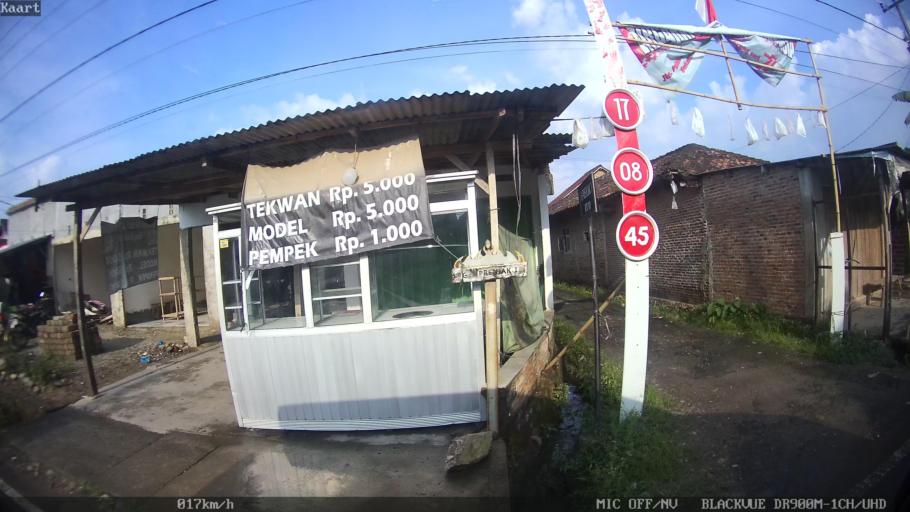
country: ID
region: Lampung
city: Kedaton
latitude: -5.3929
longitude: 105.3156
